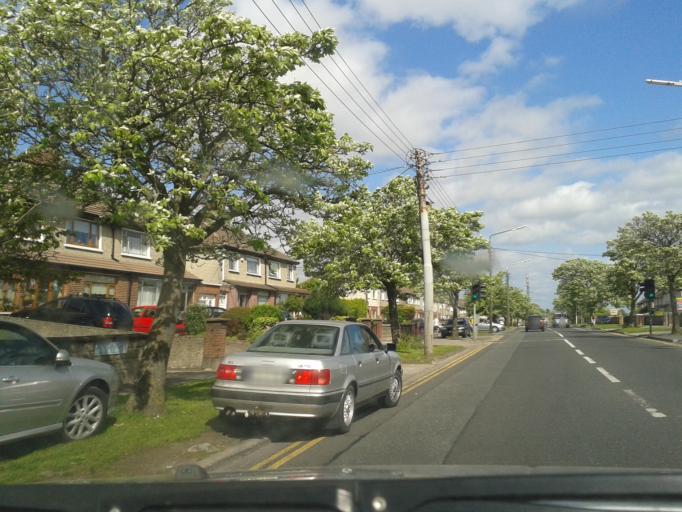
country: IE
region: Leinster
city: Ballymun
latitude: 53.3900
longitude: -6.2711
